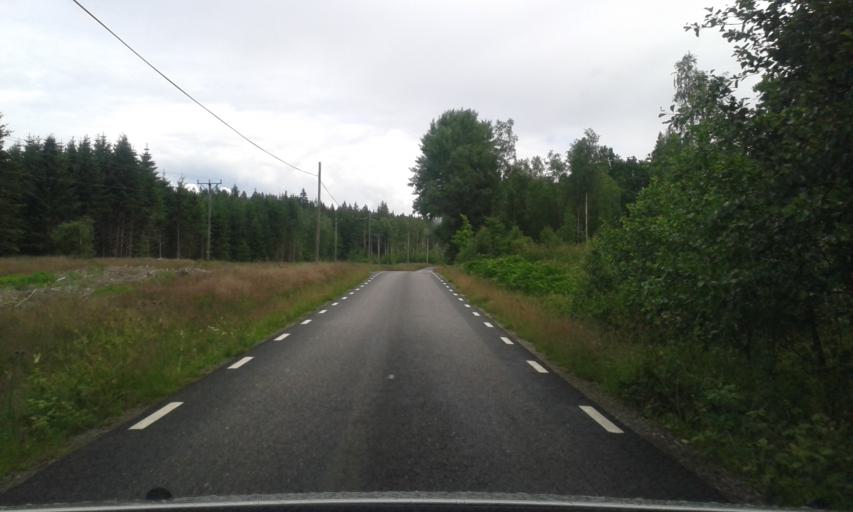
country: SE
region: Vaestra Goetaland
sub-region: Kungalvs Kommun
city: Diserod
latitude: 57.9613
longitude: 11.9617
